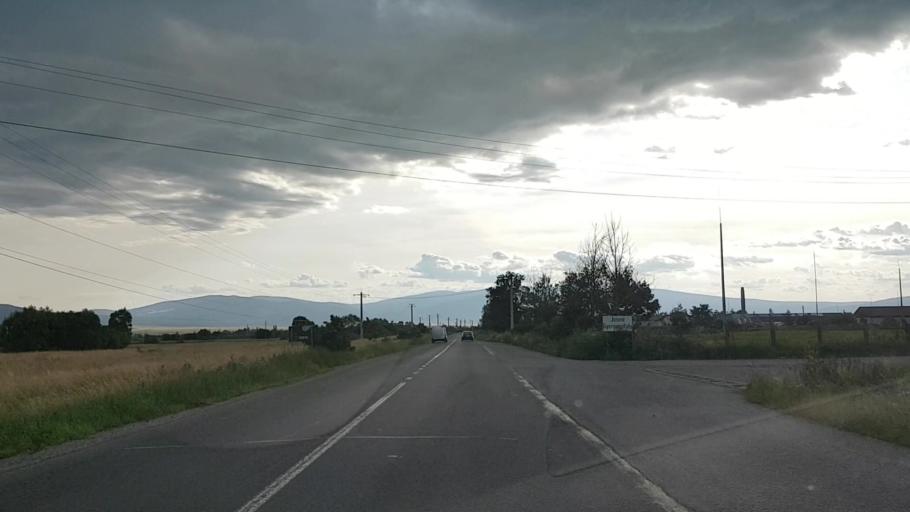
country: RO
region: Harghita
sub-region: Comuna Ciumani
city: Ciumani
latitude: 46.7083
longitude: 25.5419
